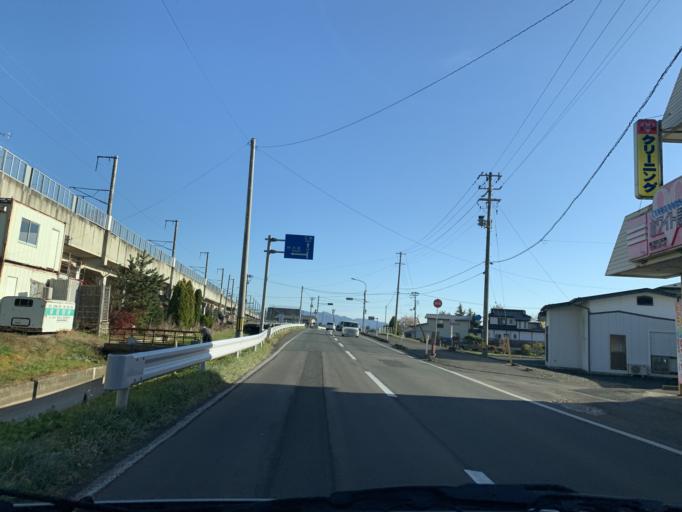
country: JP
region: Iwate
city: Kitakami
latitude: 39.2192
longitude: 141.1332
